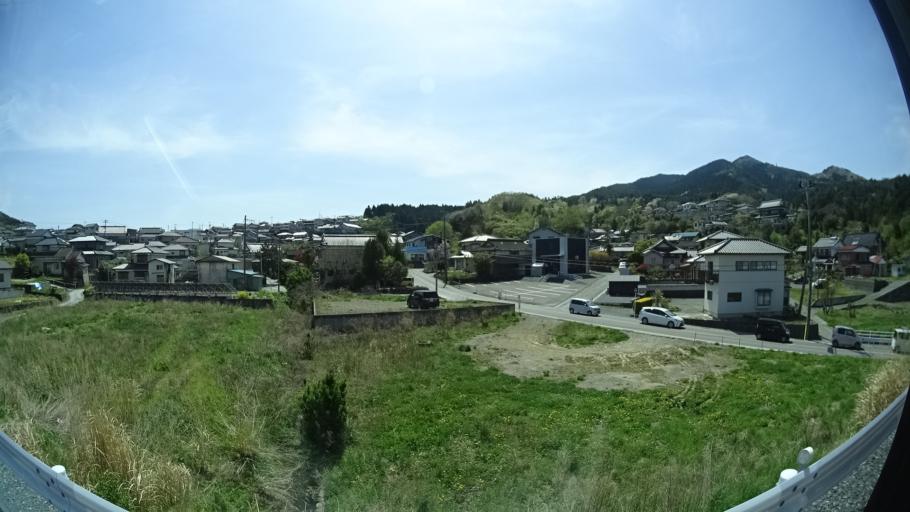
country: JP
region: Iwate
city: Ofunato
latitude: 39.0139
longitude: 141.7153
